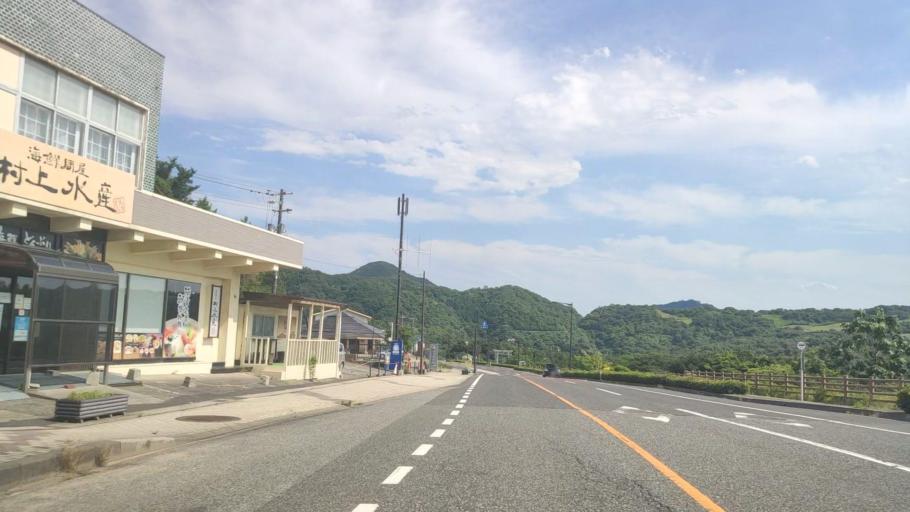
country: JP
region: Tottori
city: Tottori
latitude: 35.5408
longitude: 134.2366
